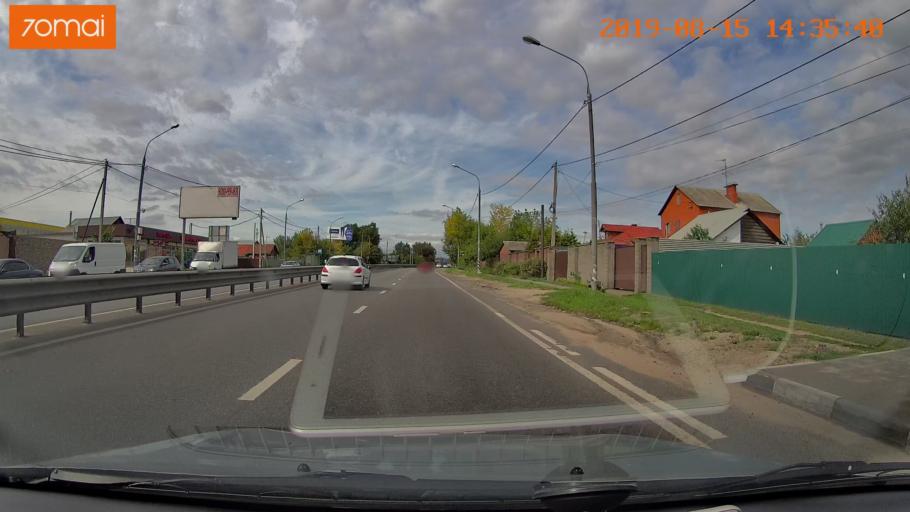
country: RU
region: Moskovskaya
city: Tomilino
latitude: 55.6401
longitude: 37.9374
